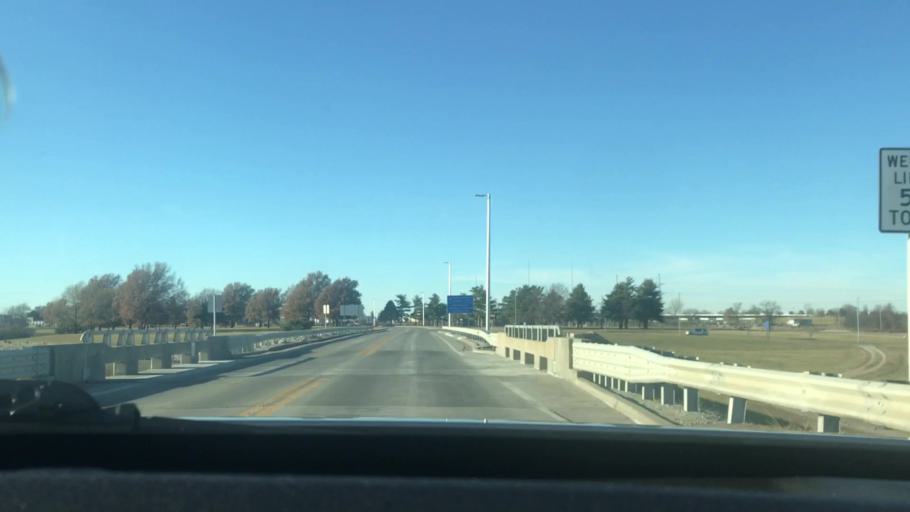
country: US
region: Missouri
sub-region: Platte County
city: Weatherby Lake
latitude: 39.3103
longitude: -94.7093
